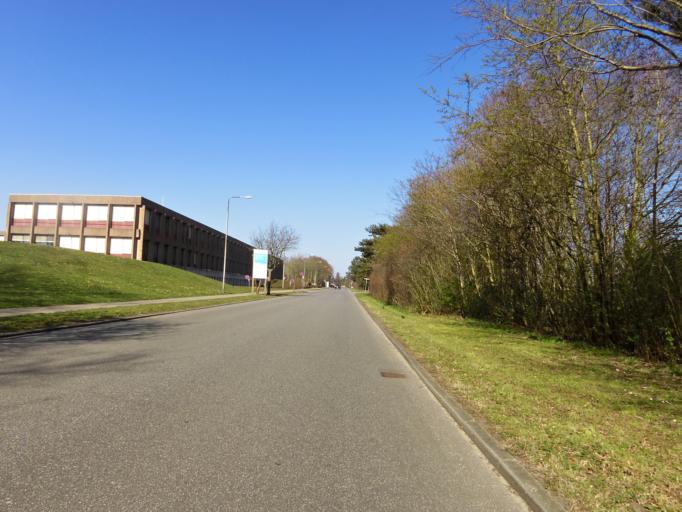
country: DK
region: South Denmark
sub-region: Esbjerg Kommune
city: Ribe
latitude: 55.3511
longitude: 8.7868
